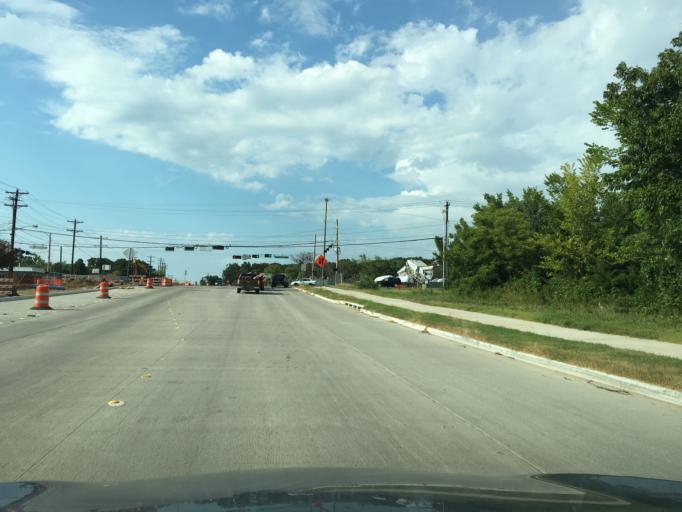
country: US
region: Texas
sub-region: Denton County
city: Denton
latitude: 33.2094
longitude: -97.0836
